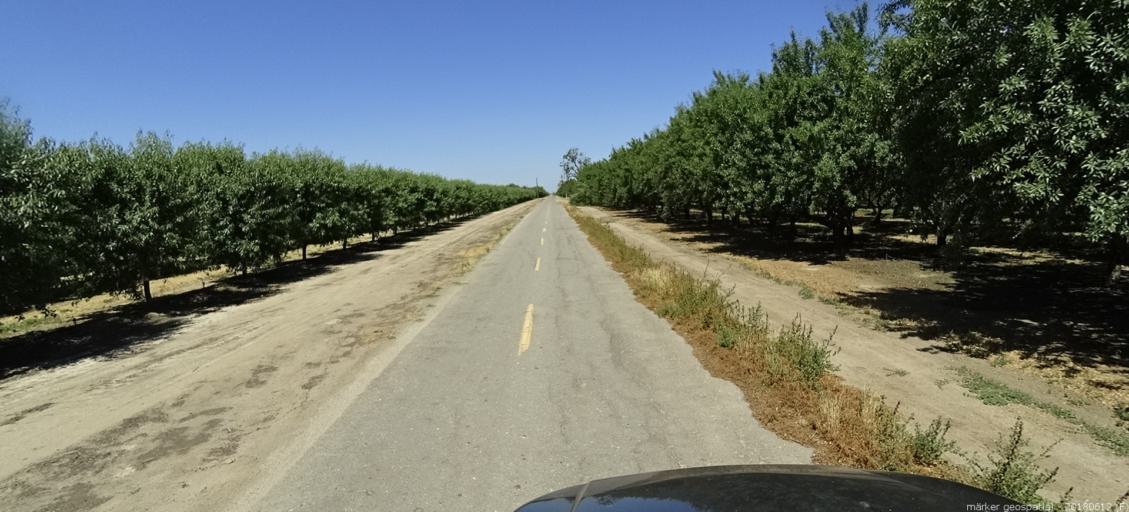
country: US
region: California
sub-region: Madera County
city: Chowchilla
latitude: 37.0472
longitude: -120.3312
